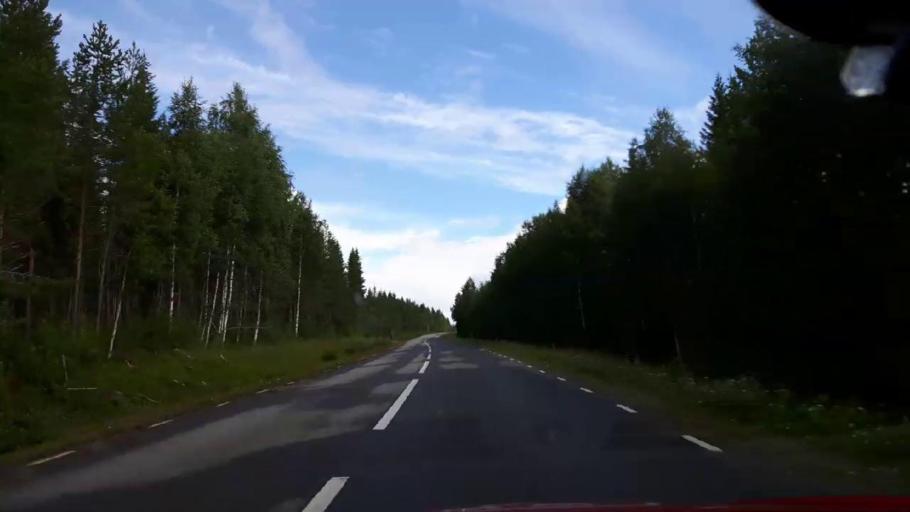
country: SE
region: Jaemtland
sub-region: Stroemsunds Kommun
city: Stroemsund
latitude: 64.3468
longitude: 15.0854
